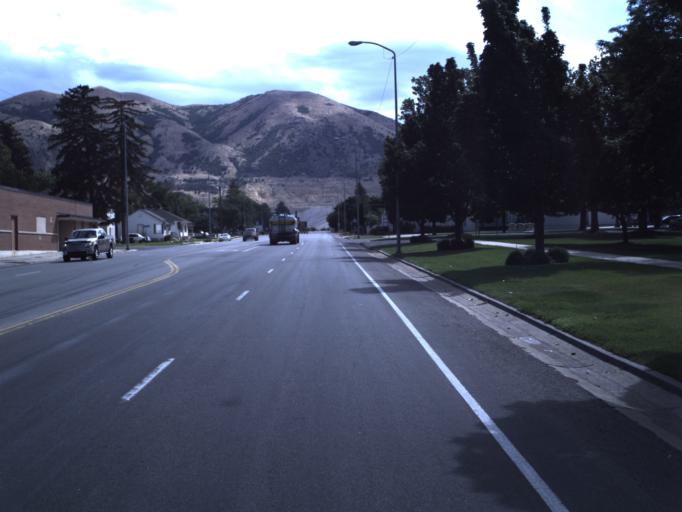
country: US
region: Utah
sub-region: Box Elder County
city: Brigham City
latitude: 41.5060
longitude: -112.0155
